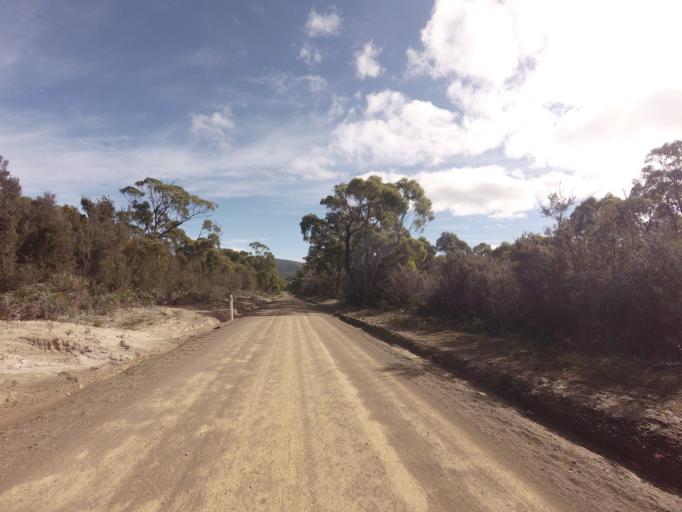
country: AU
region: Tasmania
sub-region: Clarence
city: Sandford
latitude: -43.0865
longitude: 147.6938
